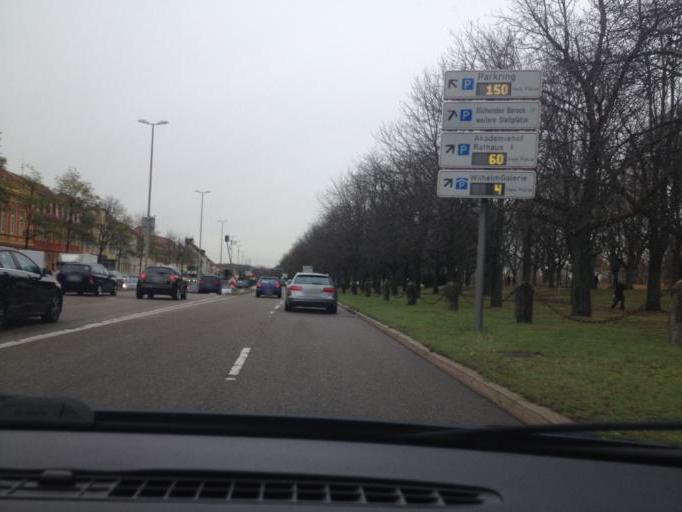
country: DE
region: Baden-Wuerttemberg
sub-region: Regierungsbezirk Stuttgart
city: Ludwigsburg
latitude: 48.8937
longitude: 9.1943
